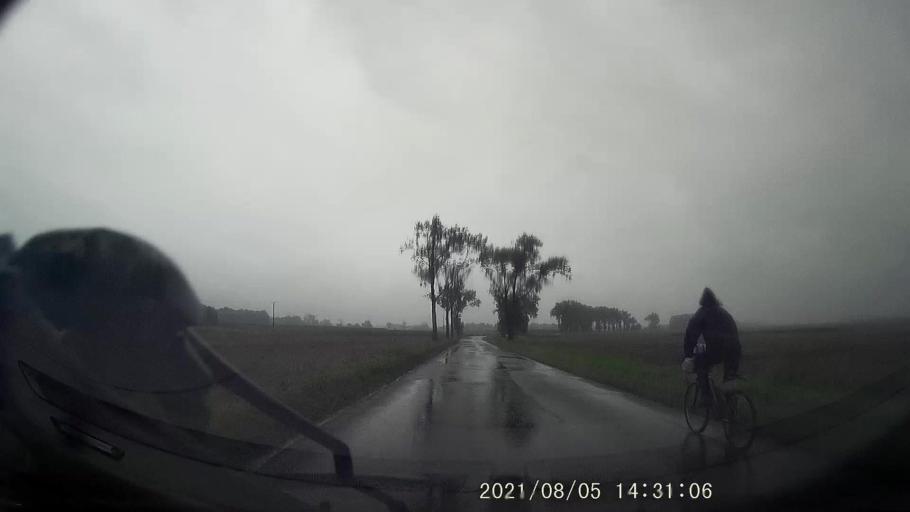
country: PL
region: Opole Voivodeship
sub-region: Powiat nyski
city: Korfantow
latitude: 50.4782
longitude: 17.5581
